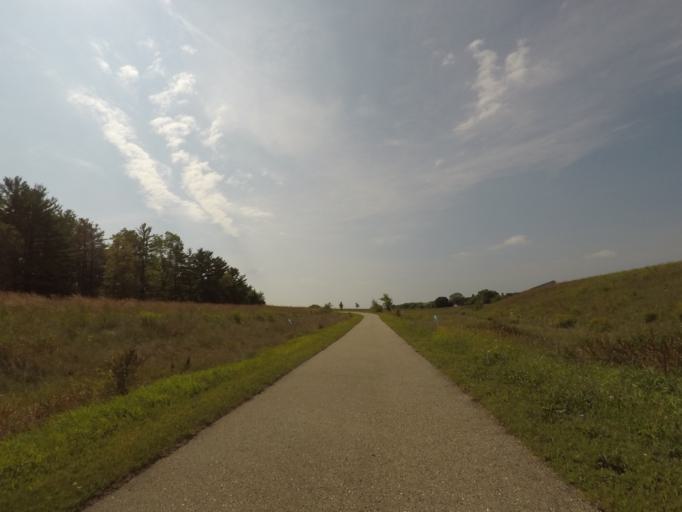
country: US
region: Wisconsin
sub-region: Jefferson County
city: Jefferson
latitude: 42.9866
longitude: -88.8293
